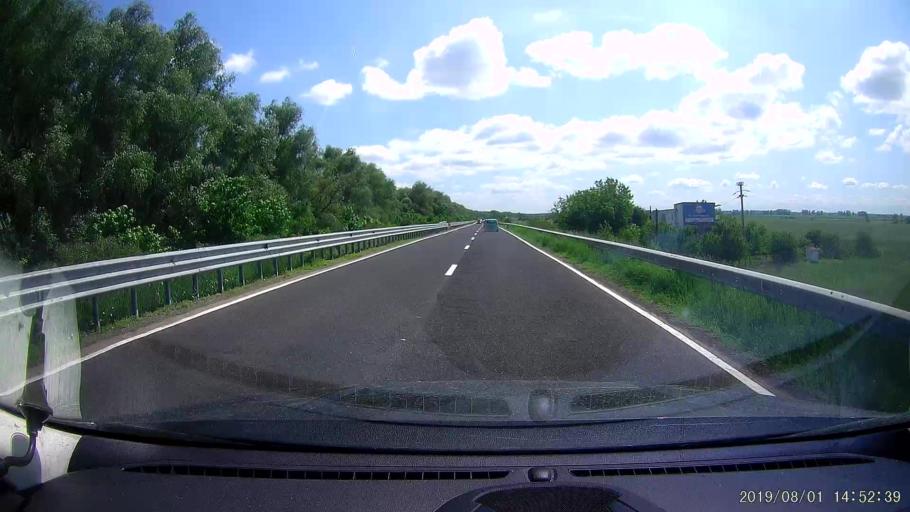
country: RO
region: Braila
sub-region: Comuna Vadeni
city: Vadeni
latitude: 45.3508
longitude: 28.0095
